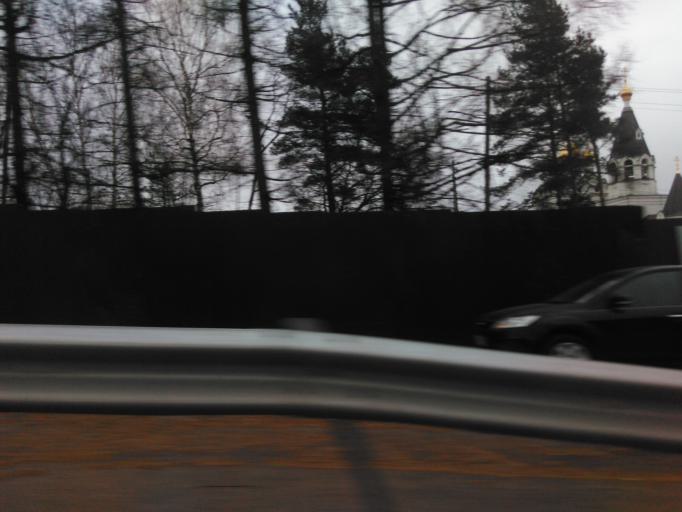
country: RU
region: Moskovskaya
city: Ashukino
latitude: 56.1281
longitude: 37.9754
